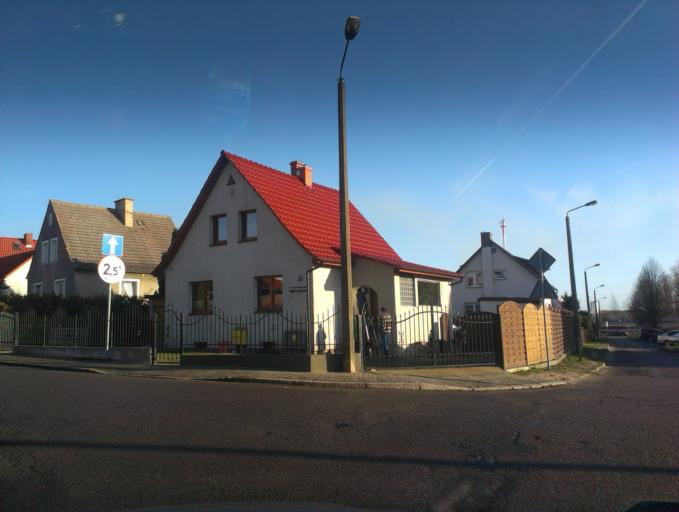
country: PL
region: West Pomeranian Voivodeship
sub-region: Powiat szczecinecki
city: Szczecinek
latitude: 53.6998
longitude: 16.7042
